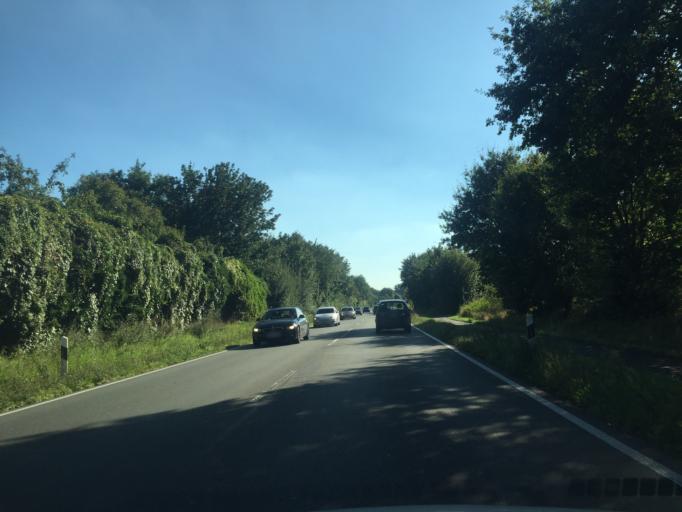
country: DE
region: North Rhine-Westphalia
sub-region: Regierungsbezirk Munster
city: Telgte
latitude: 51.9852
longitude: 7.7744
